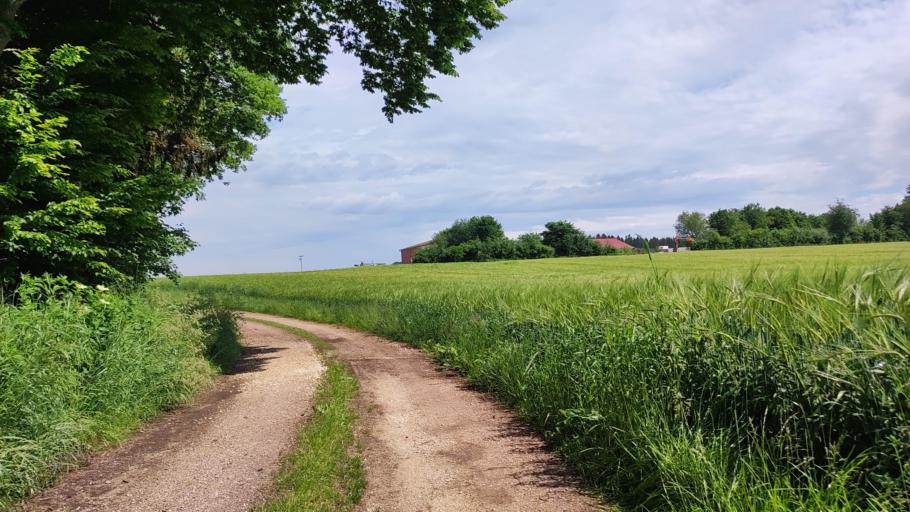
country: DE
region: Bavaria
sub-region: Swabia
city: Landensberg
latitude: 48.4327
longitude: 10.5335
